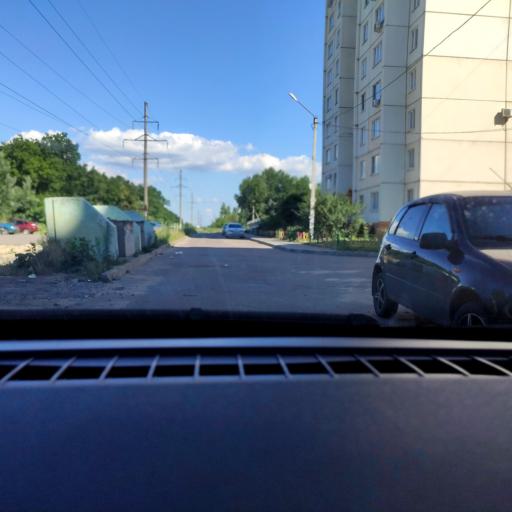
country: RU
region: Voronezj
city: Podgornoye
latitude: 51.7320
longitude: 39.2040
